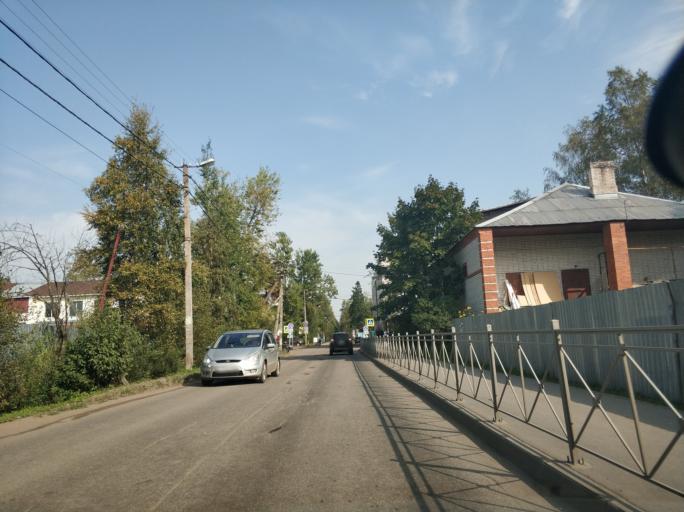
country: RU
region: Leningrad
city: Vsevolozhsk
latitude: 60.0202
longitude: 30.6785
